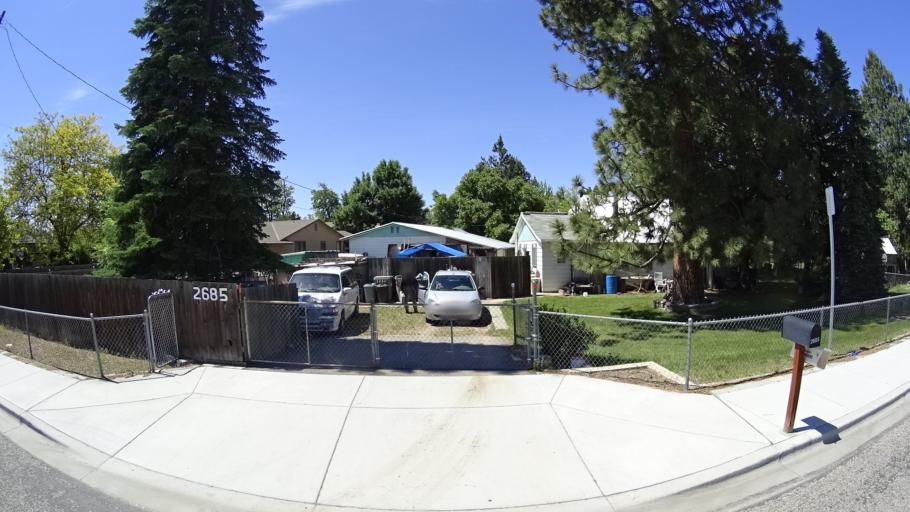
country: US
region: Idaho
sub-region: Ada County
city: Boise
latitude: 43.5687
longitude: -116.1498
